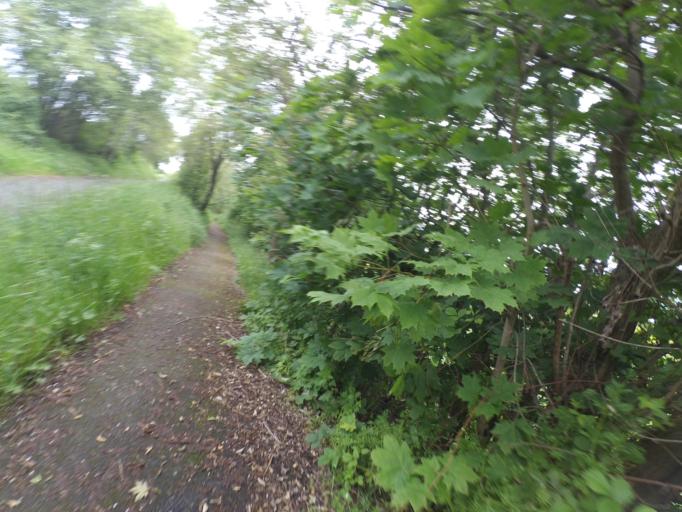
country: GB
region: Scotland
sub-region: East Lothian
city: Musselburgh
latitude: 55.9183
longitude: -3.0326
